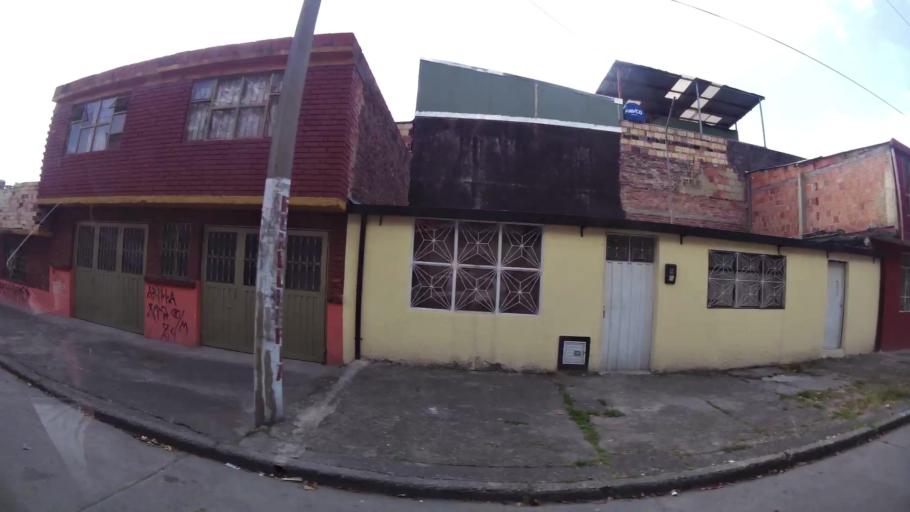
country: CO
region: Bogota D.C.
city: Bogota
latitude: 4.5472
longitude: -74.0940
